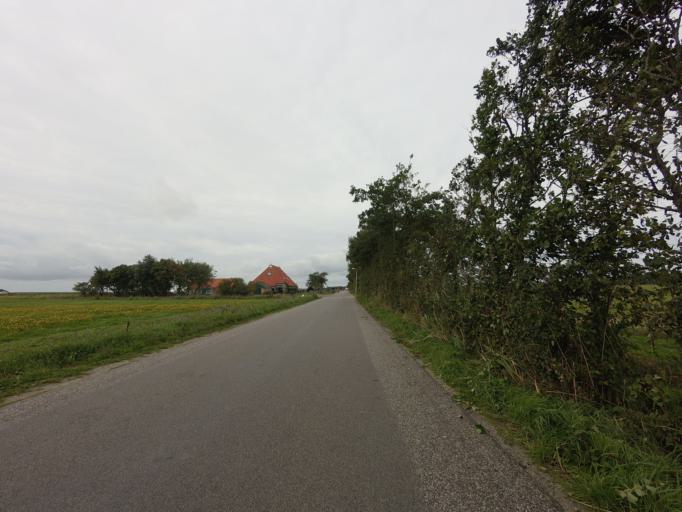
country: NL
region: Friesland
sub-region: Gemeente Ameland
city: Nes
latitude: 53.4404
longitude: 5.7087
